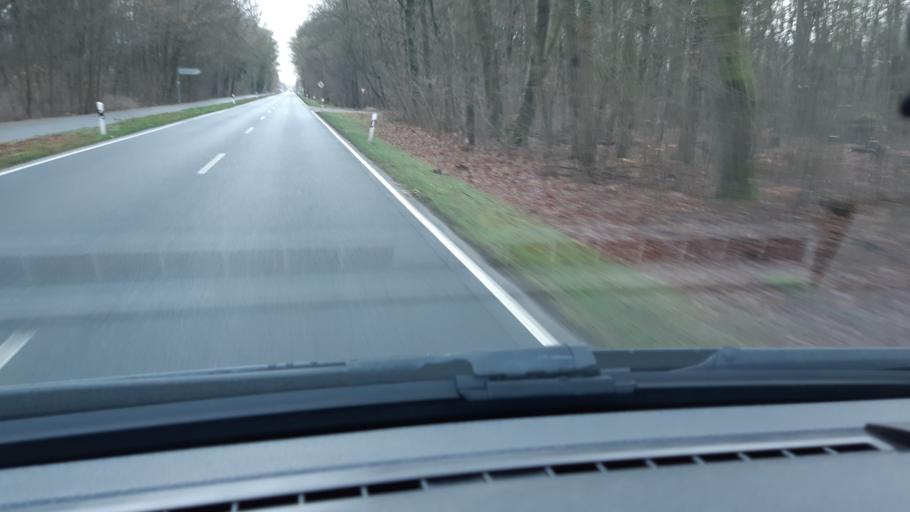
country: DE
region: Brandenburg
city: Zehdenick
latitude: 53.0009
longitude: 13.3494
